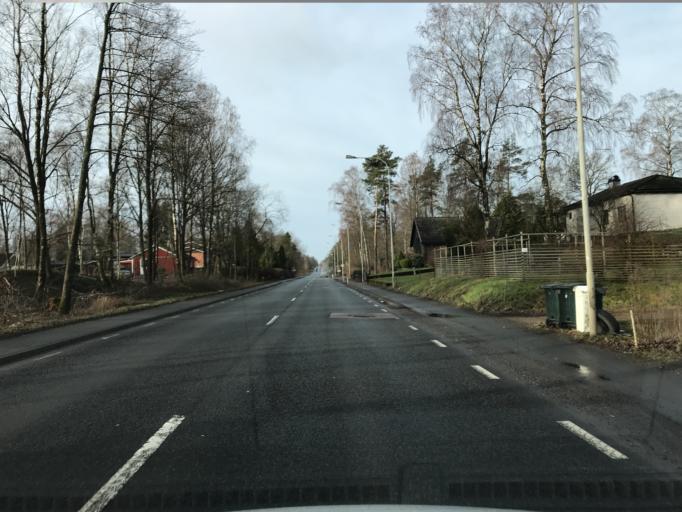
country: SE
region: Skane
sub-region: Perstorps Kommun
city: Perstorp
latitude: 56.1366
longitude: 13.4217
